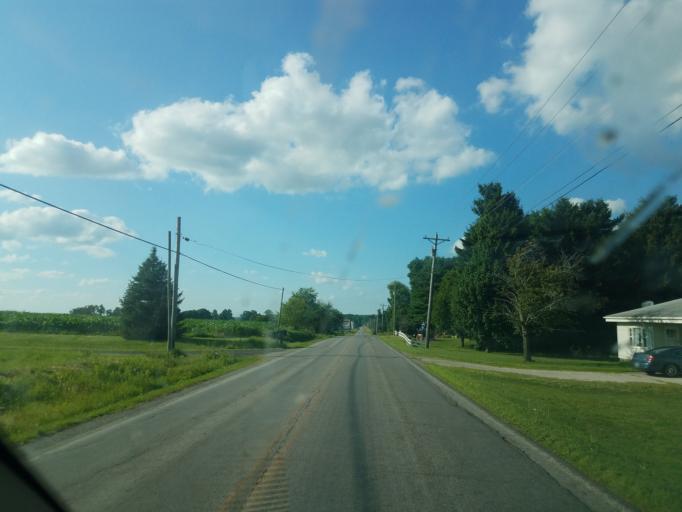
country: US
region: Ohio
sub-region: Wayne County
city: Apple Creek
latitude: 40.7444
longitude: -81.8960
